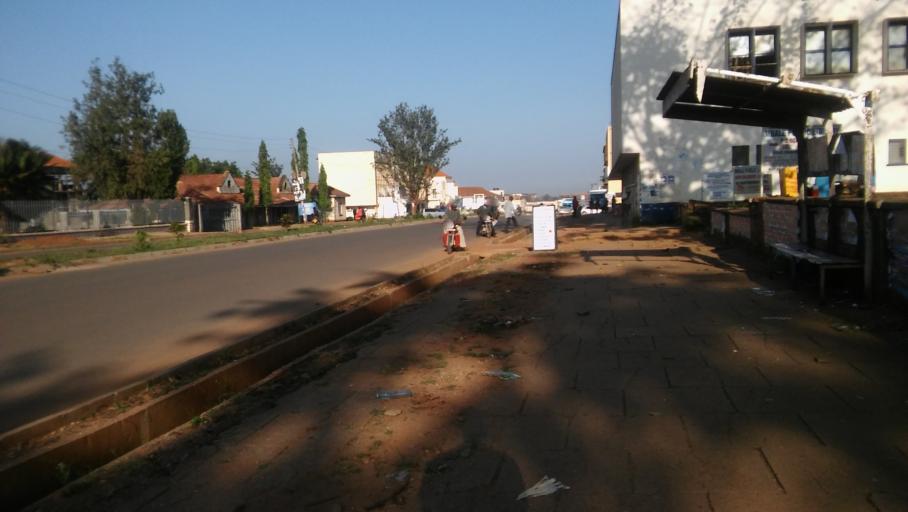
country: UG
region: Eastern Region
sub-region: Mbale District
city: Mbale
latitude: 1.0708
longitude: 34.1831
